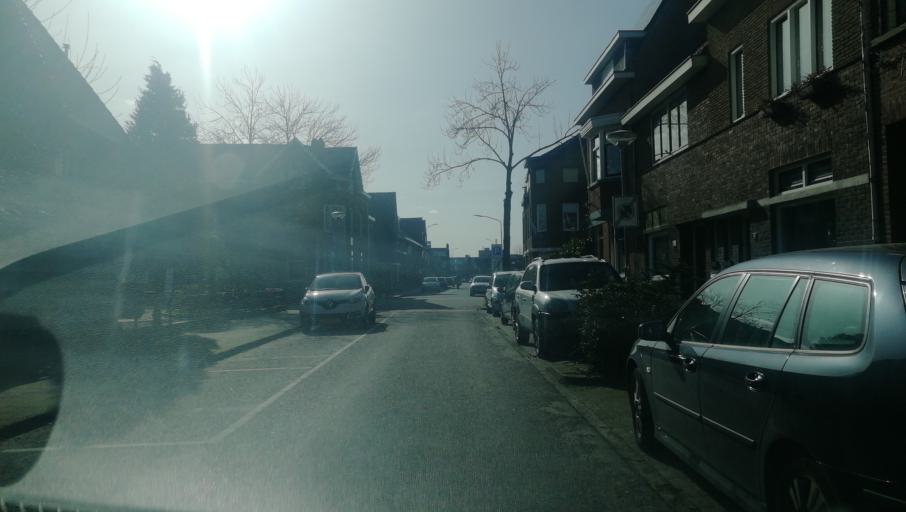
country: NL
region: Limburg
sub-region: Gemeente Venlo
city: Venlo
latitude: 51.3634
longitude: 6.1644
